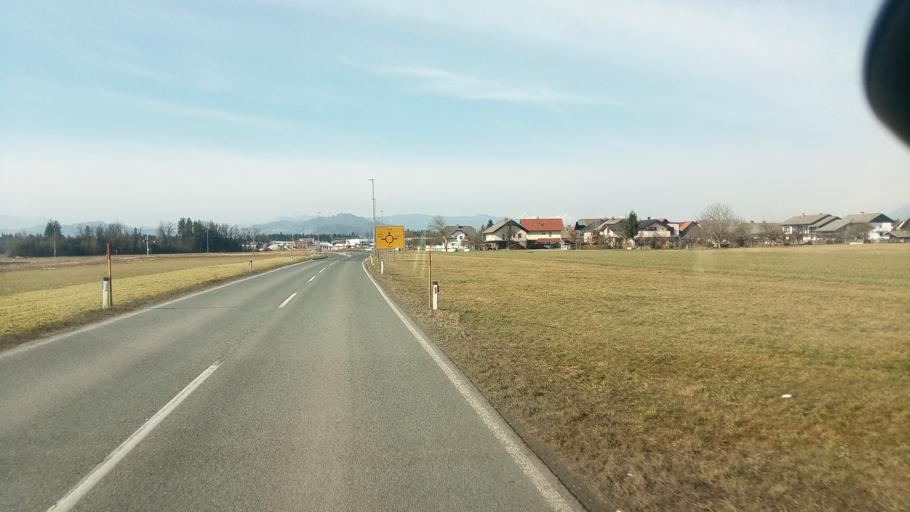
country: SI
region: Sencur
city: Sencur
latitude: 46.2366
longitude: 14.4221
